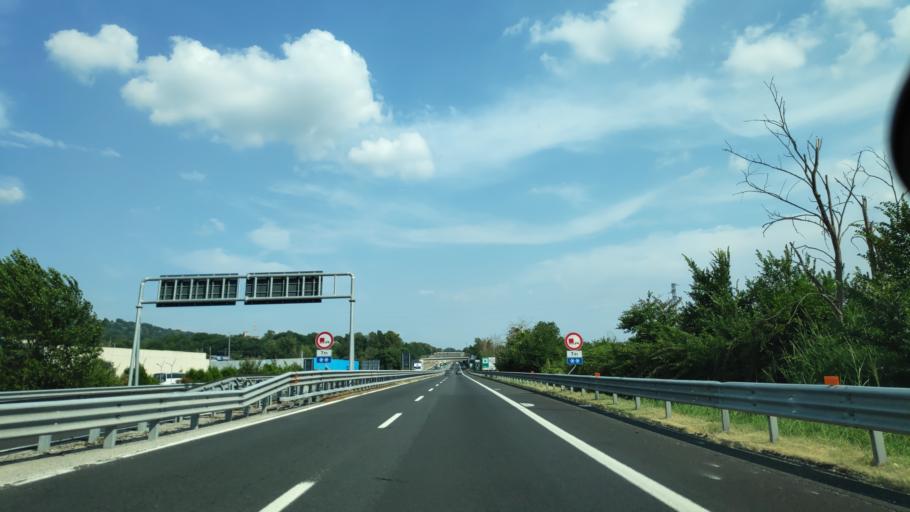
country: IT
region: Umbria
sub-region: Provincia di Terni
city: Attigliano
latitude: 42.5067
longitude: 12.2986
